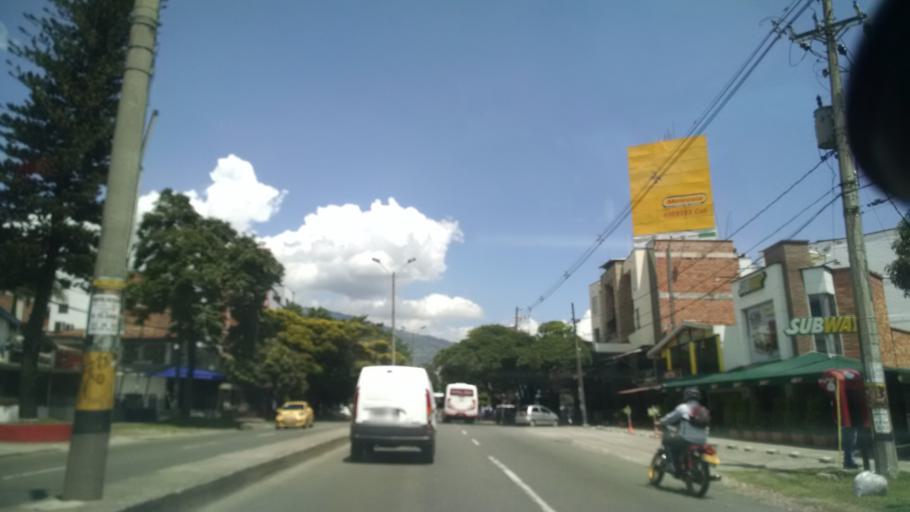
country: CO
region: Antioquia
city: Medellin
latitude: 6.2400
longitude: -75.6029
